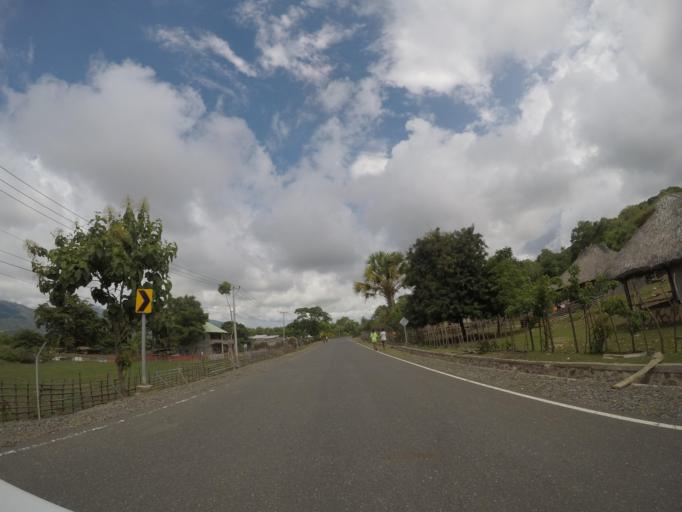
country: TL
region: Liquica
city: Maubara
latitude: -8.7445
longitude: 125.1112
